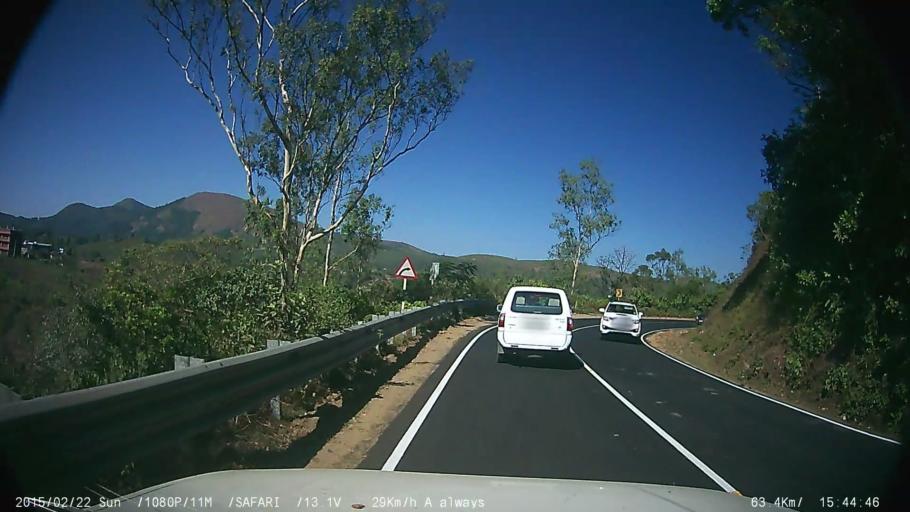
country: IN
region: Kerala
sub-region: Kottayam
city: Erattupetta
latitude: 9.5809
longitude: 76.9750
